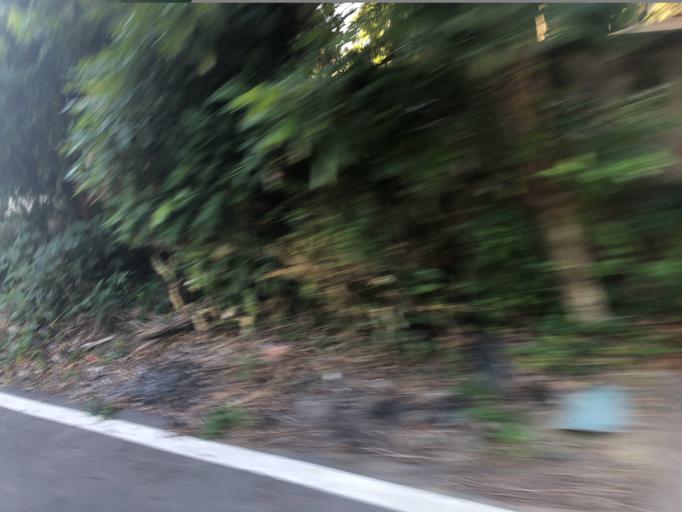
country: TW
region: Taiwan
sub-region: Hsinchu
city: Hsinchu
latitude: 24.7447
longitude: 120.9762
